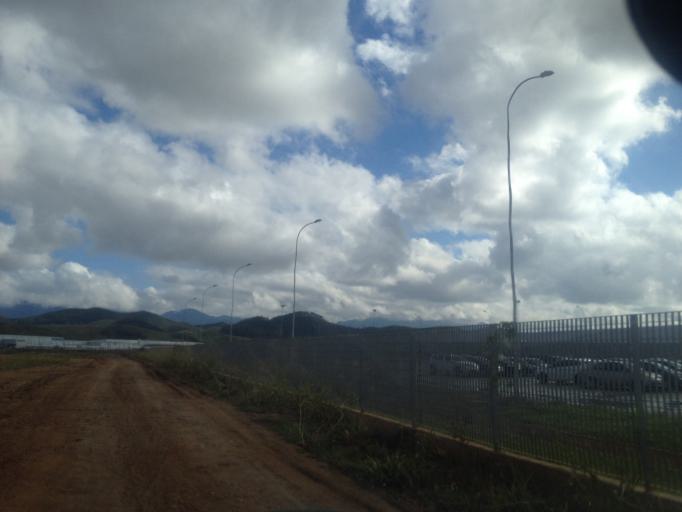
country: BR
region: Rio de Janeiro
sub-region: Resende
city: Resende
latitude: -22.4380
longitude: -44.3852
